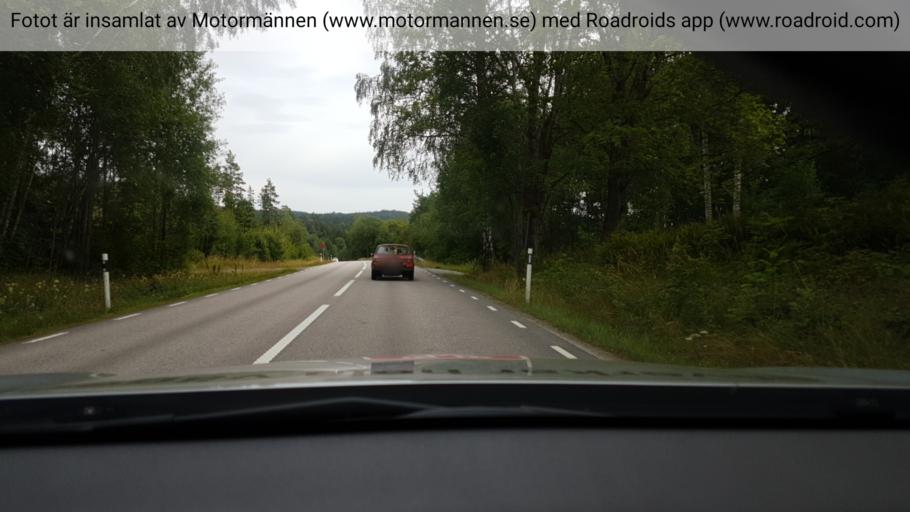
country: SE
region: Vaestra Goetaland
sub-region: Bengtsfors Kommun
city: Billingsfors
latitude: 58.9242
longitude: 12.2165
